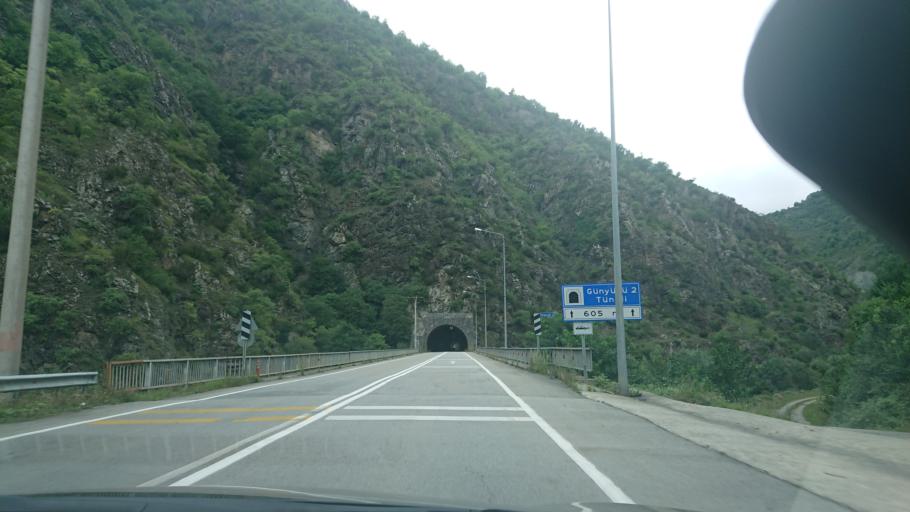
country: TR
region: Gumushane
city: Kurtun
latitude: 40.7344
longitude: 39.0034
